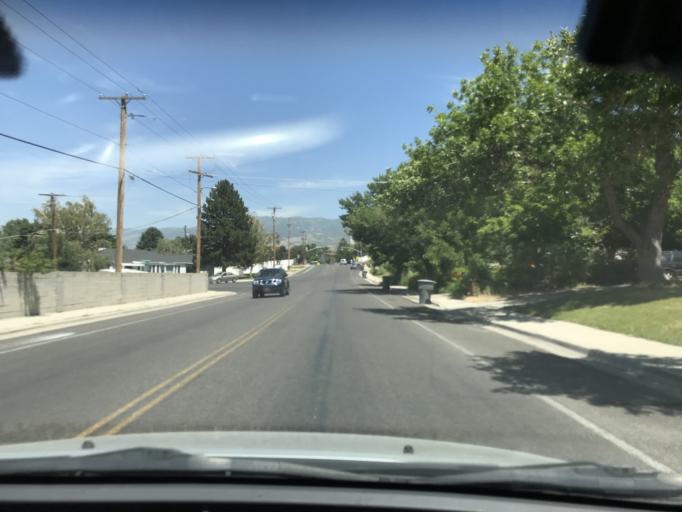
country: US
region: Utah
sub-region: Davis County
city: North Salt Lake
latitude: 40.8479
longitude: -111.8981
